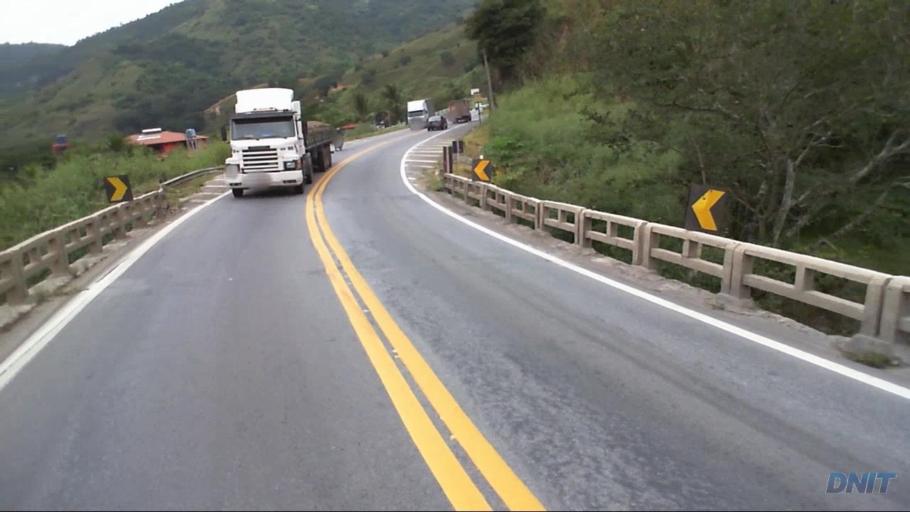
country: BR
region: Minas Gerais
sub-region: Timoteo
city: Timoteo
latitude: -19.6166
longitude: -42.7825
